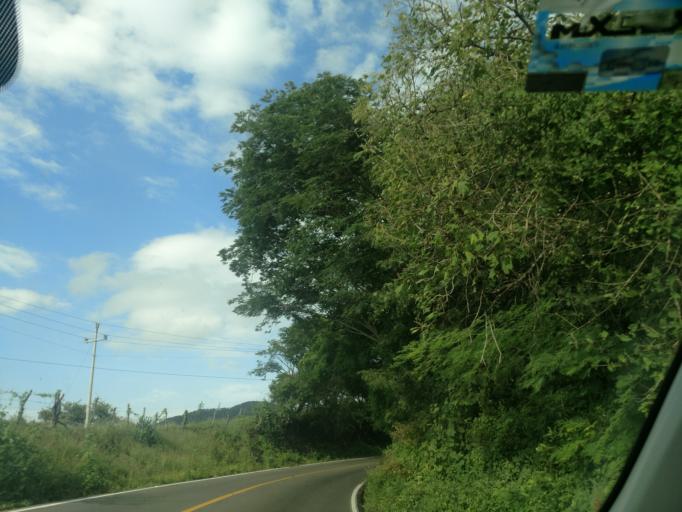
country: MX
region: Jalisco
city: Ameca
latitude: 20.5273
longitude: -104.2103
